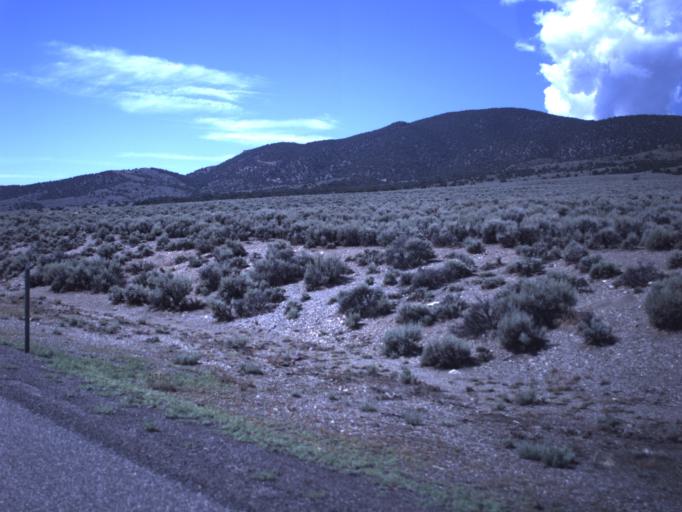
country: US
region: Utah
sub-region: Piute County
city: Junction
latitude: 38.3648
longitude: -112.2239
